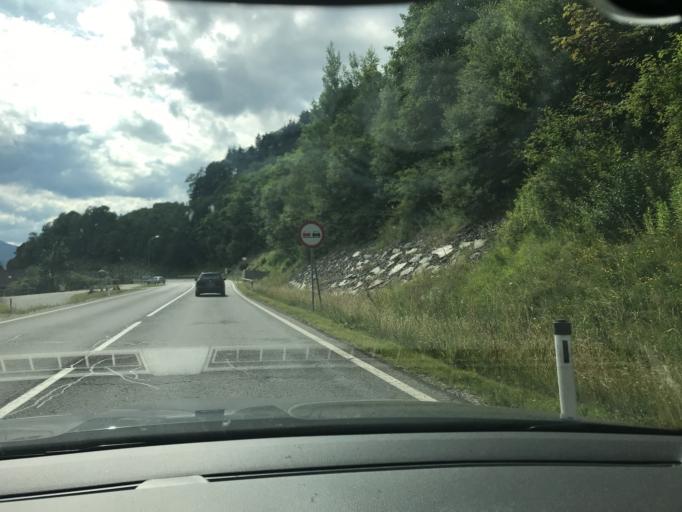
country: AT
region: Tyrol
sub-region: Politischer Bezirk Lienz
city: Abfaltersbach
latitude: 46.7596
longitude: 12.5403
